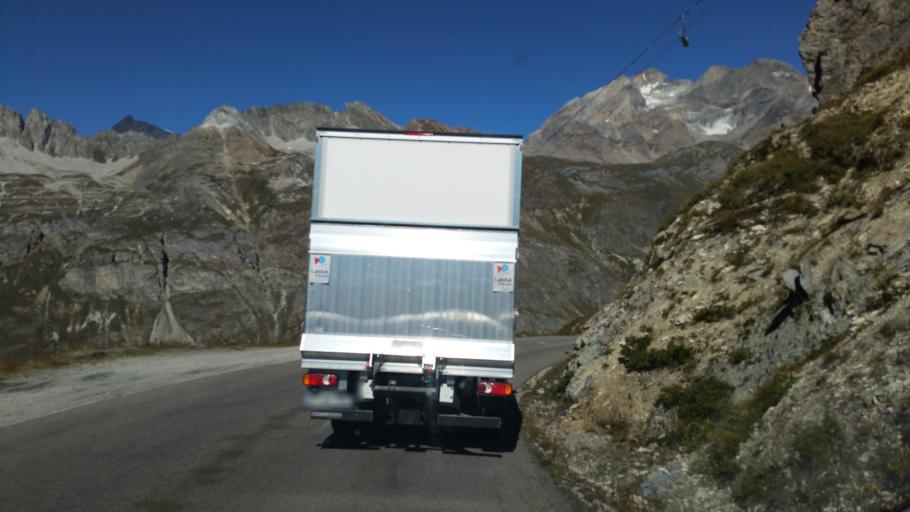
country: FR
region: Rhone-Alpes
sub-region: Departement de la Savoie
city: Val-d'Isere
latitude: 45.4388
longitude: 7.0051
